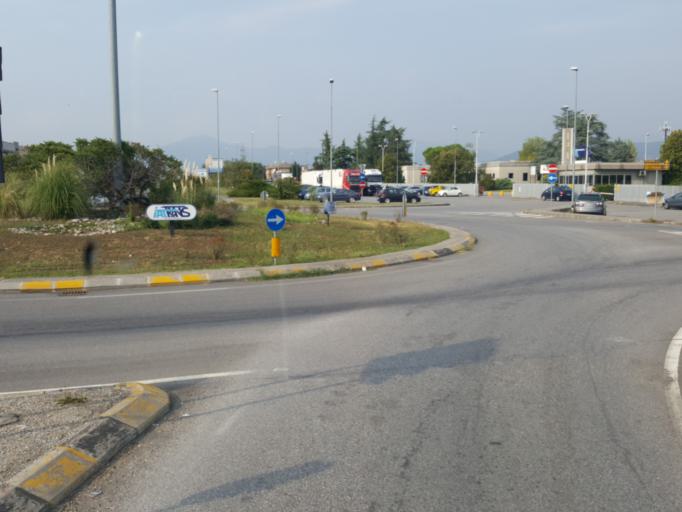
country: IT
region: Lombardy
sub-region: Provincia di Bergamo
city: Calcinate
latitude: 45.6166
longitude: 9.8073
